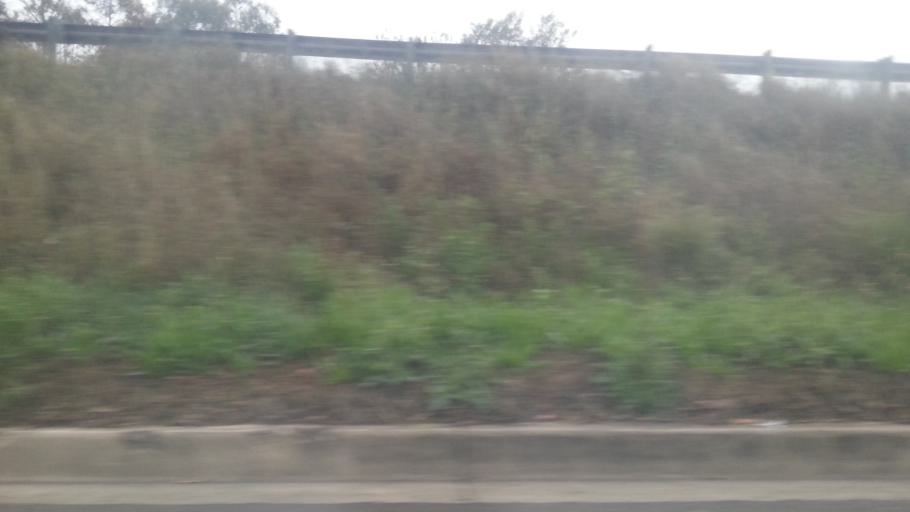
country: AU
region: New South Wales
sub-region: Camden
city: Narellan Vale
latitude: -34.0414
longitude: 150.7445
